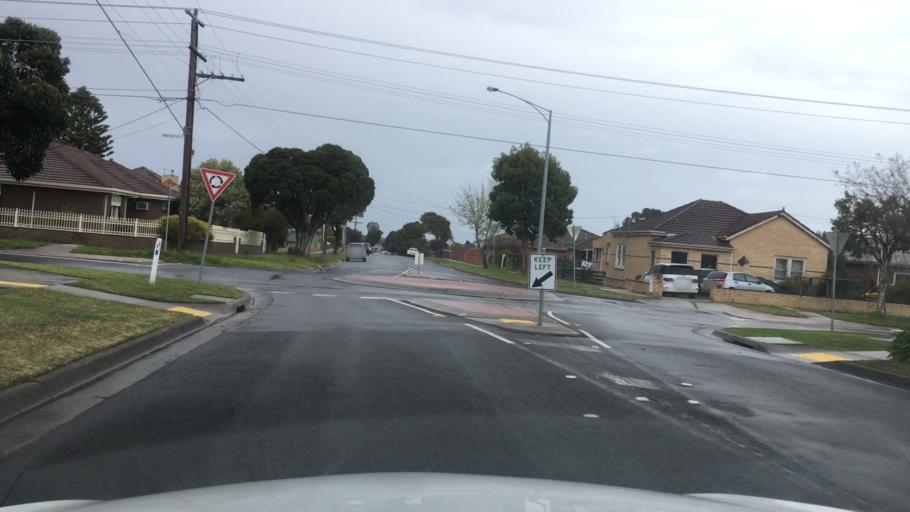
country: AU
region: Victoria
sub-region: Greater Dandenong
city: Springvale
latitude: -37.9508
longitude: 145.1449
